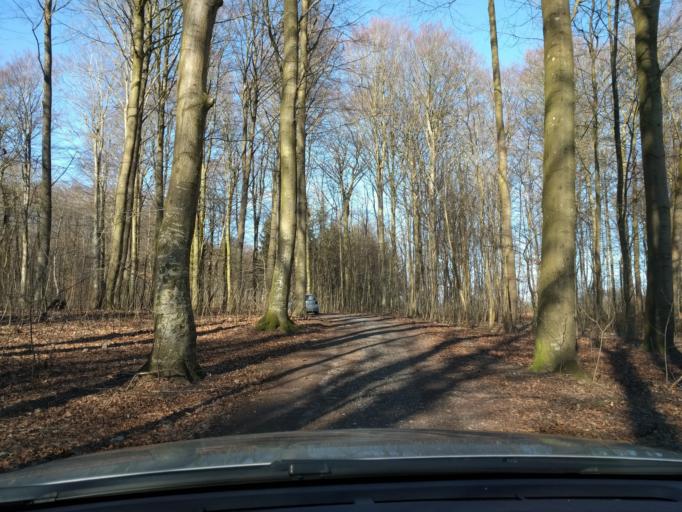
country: DK
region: South Denmark
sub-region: Aabenraa Kommune
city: Lojt Kirkeby
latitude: 55.1276
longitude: 9.5161
